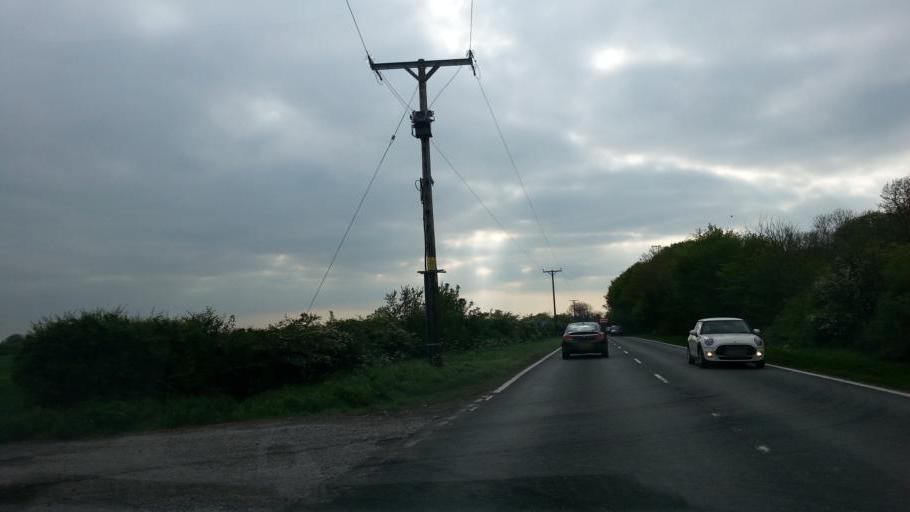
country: GB
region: England
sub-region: Nottinghamshire
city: South Collingham
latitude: 53.0700
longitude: -0.6664
